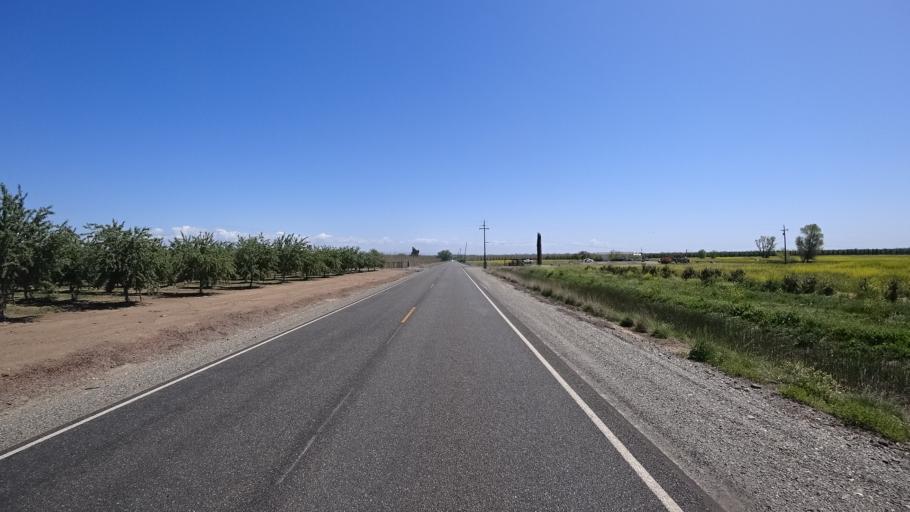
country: US
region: California
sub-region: Glenn County
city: Hamilton City
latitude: 39.7665
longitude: -122.0439
